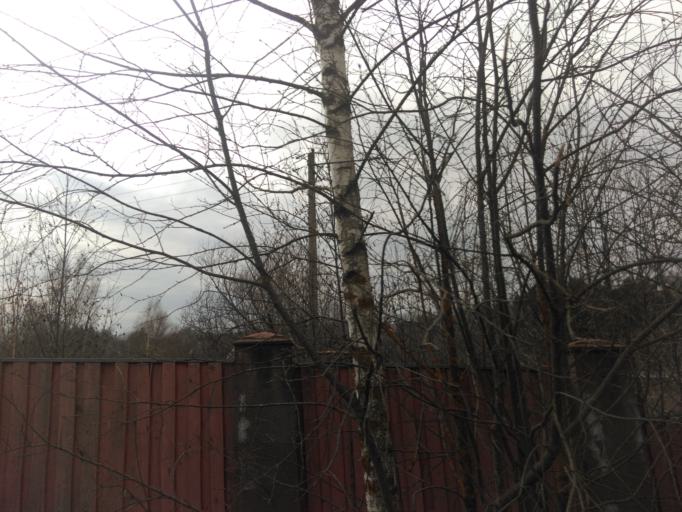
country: RU
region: Moskovskaya
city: Tuchkovo
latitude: 55.6156
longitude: 36.4203
